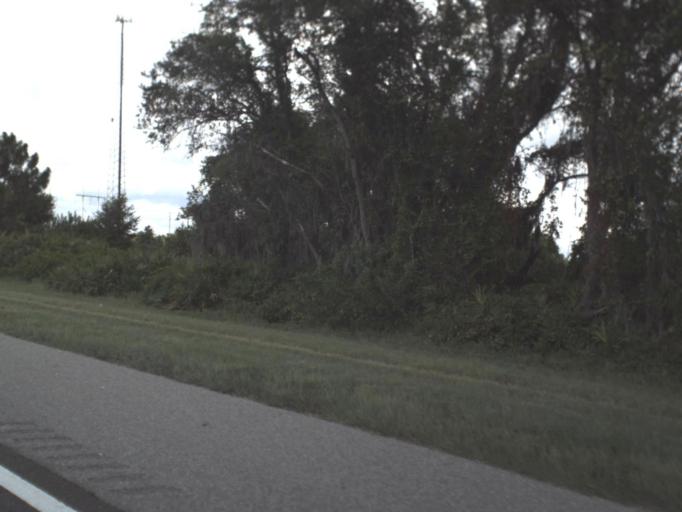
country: US
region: Florida
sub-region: Hillsborough County
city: Apollo Beach
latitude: 27.7446
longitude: -82.3818
